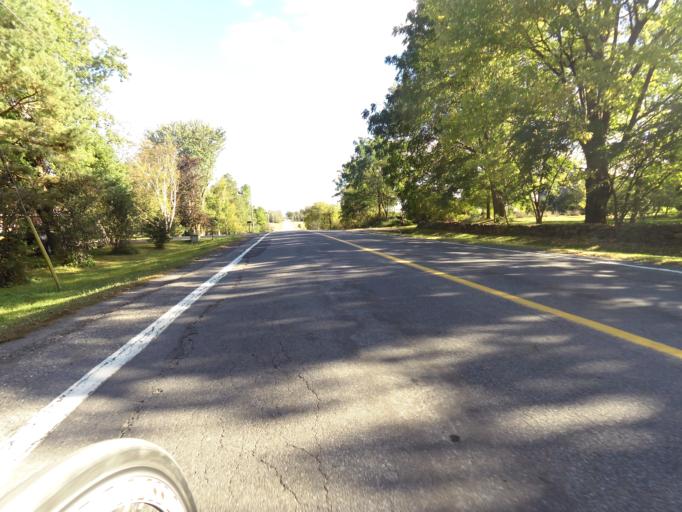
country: CA
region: Ontario
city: Bells Corners
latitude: 45.1099
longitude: -75.7235
